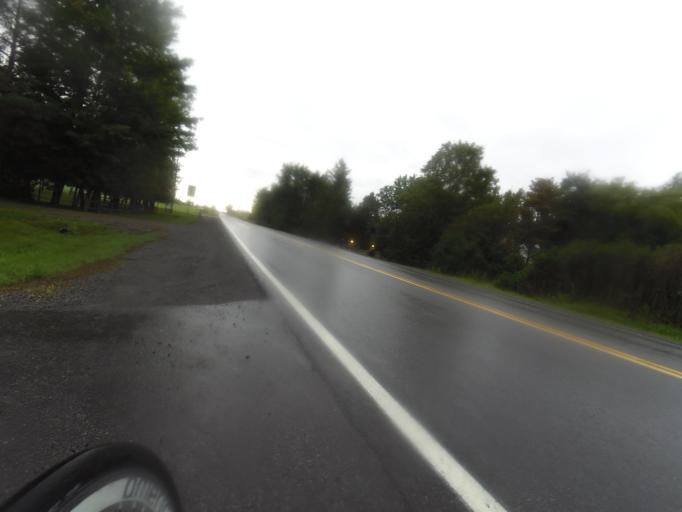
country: CA
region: Ontario
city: Bells Corners
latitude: 45.1891
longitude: -75.6795
